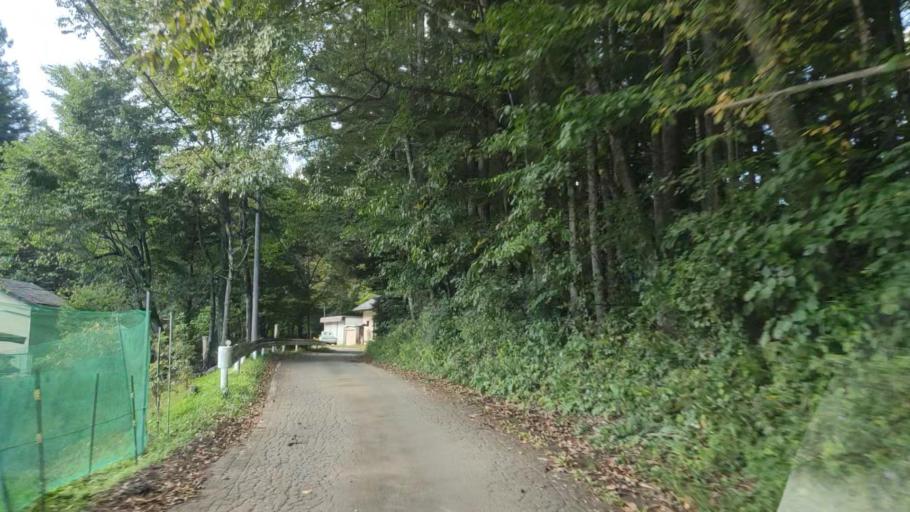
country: JP
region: Gunma
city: Nakanojomachi
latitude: 36.6575
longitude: 138.6233
